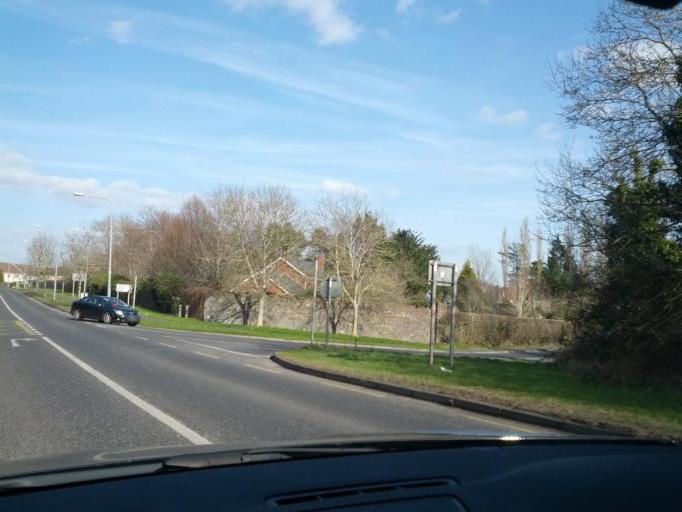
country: IE
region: Leinster
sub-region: Kildare
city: Leixlip
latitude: 53.3546
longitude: -6.4778
